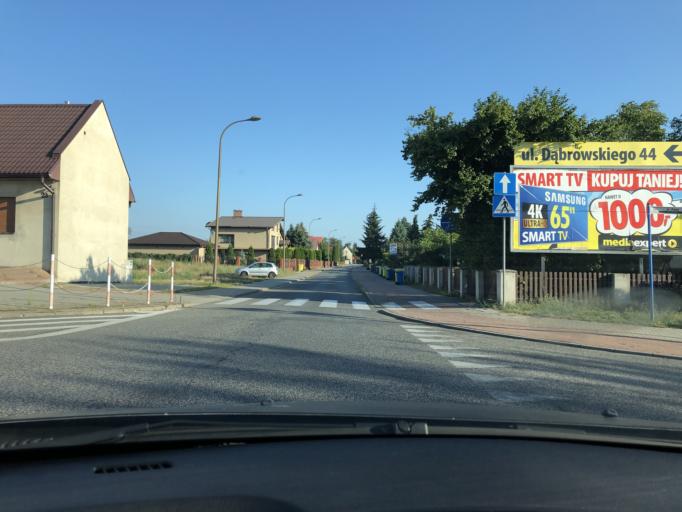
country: PL
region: Lodz Voivodeship
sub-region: Powiat wieruszowski
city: Wieruszow
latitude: 51.2914
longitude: 18.1611
